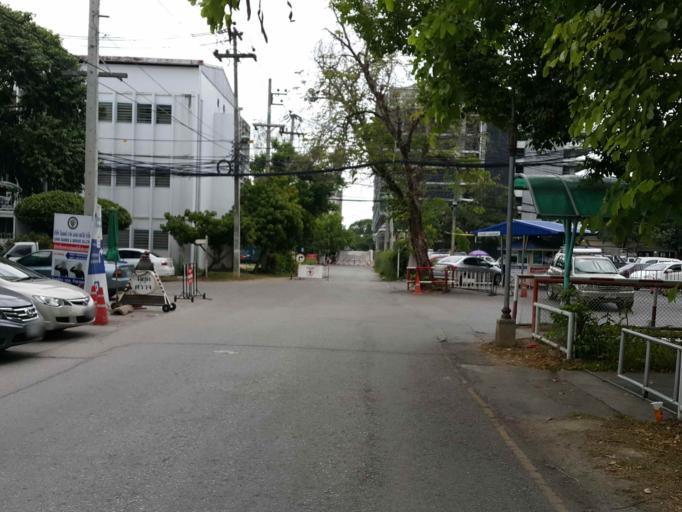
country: TH
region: Chiang Mai
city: Chiang Mai
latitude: 18.7914
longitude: 98.9710
